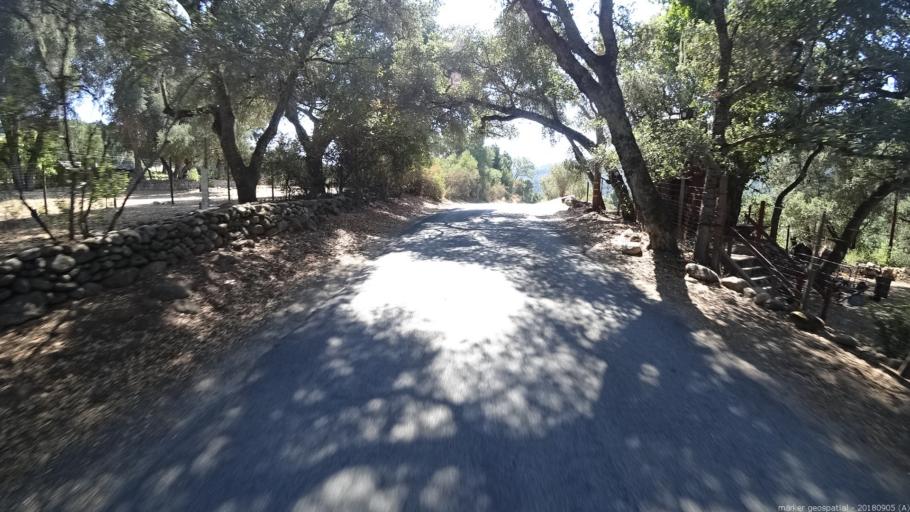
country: US
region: California
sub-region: Monterey County
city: Carmel Valley Village
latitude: 36.4032
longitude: -121.6601
